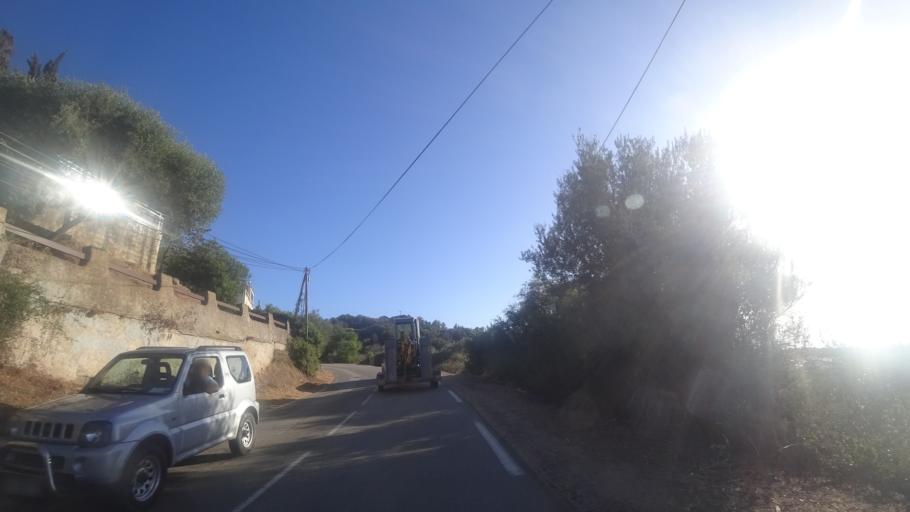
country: FR
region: Corsica
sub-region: Departement de la Corse-du-Sud
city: Cargese
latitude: 42.1397
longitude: 8.6002
